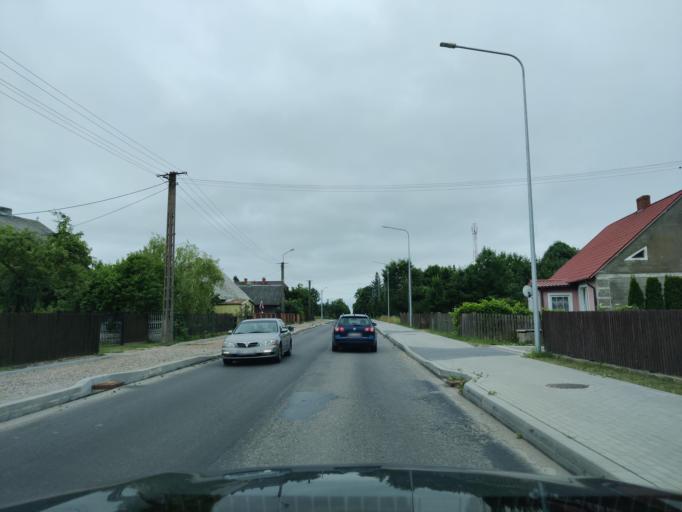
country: PL
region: Warmian-Masurian Voivodeship
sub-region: Powiat szczycienski
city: Rozogi
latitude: 53.4332
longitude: 21.3636
